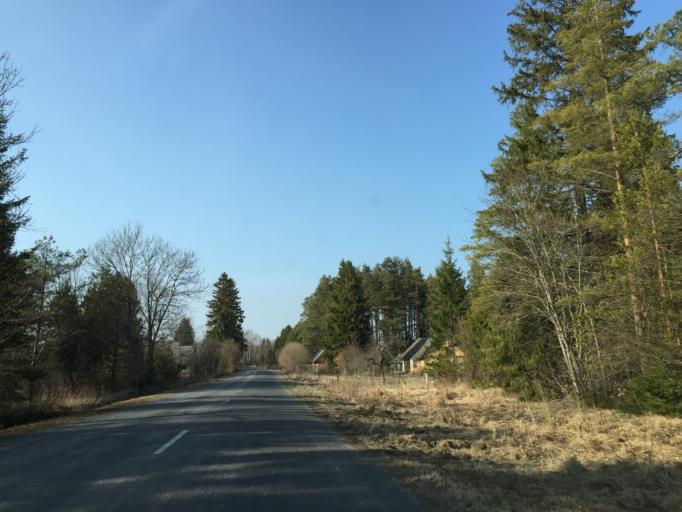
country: EE
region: Saare
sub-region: Orissaare vald
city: Orissaare
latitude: 58.6037
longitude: 23.3154
